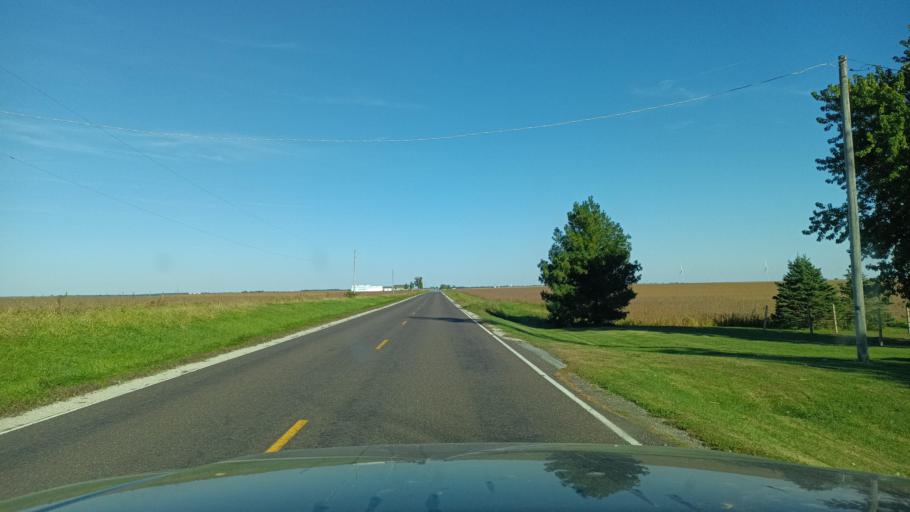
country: US
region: Illinois
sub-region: McLean County
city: Heyworth
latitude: 40.2316
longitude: -89.0571
